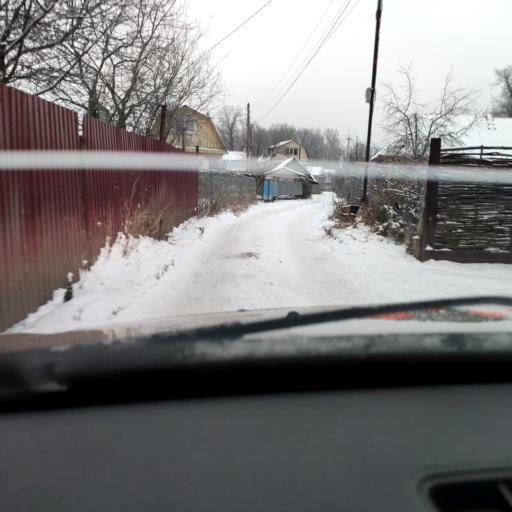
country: RU
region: Bashkortostan
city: Ufa
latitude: 54.6964
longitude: 55.8929
